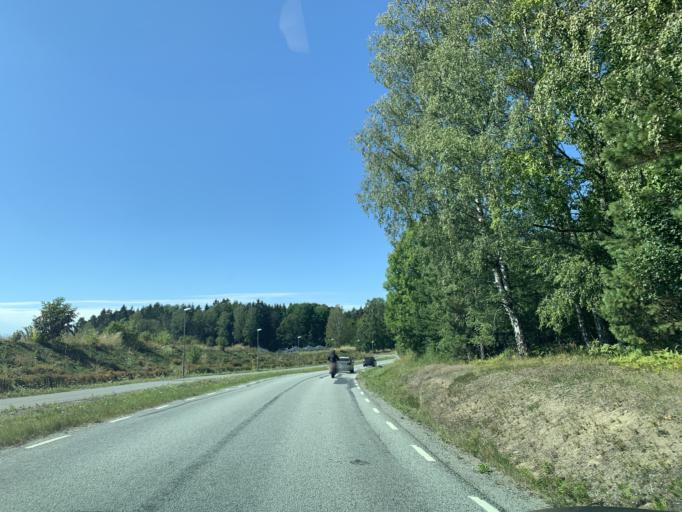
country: SE
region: Stockholm
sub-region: Ekero Kommun
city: Ekeroe
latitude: 59.2722
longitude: 17.8185
